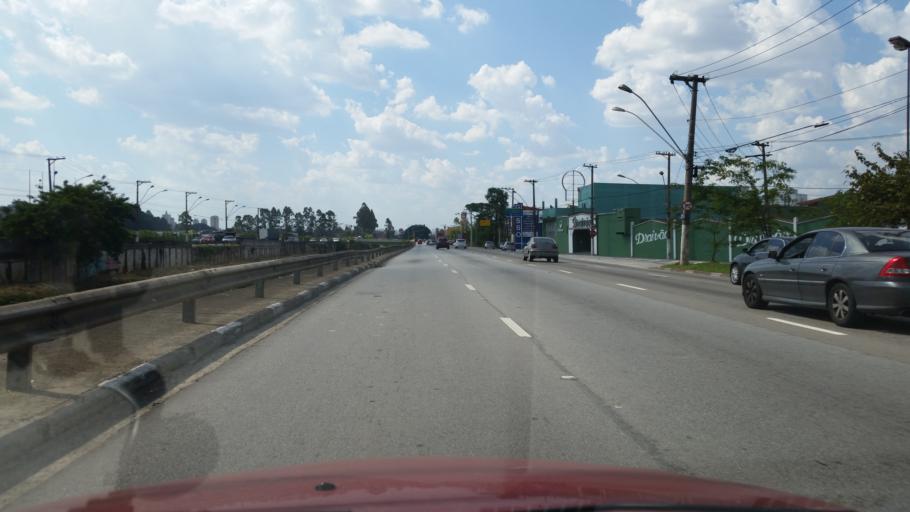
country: BR
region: Sao Paulo
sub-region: Sao Caetano Do Sul
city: Sao Caetano do Sul
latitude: -23.6351
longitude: -46.5360
